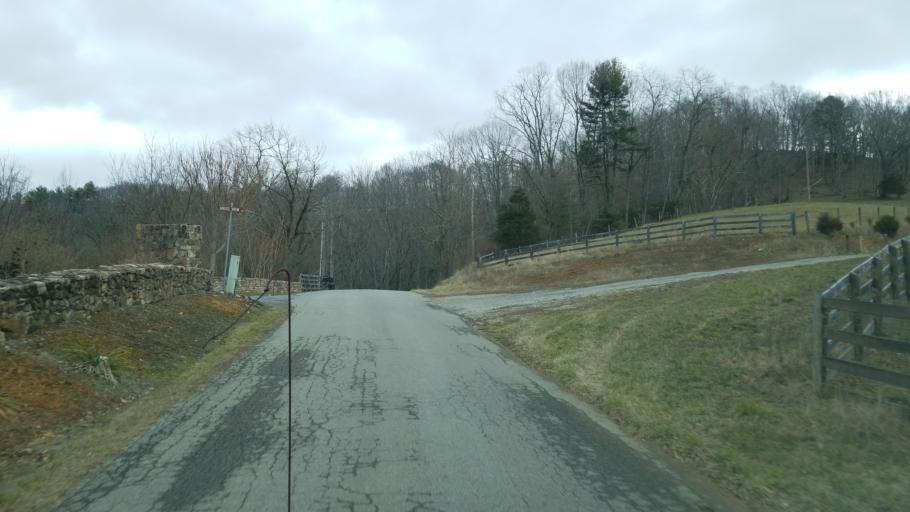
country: US
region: Virginia
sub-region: Giles County
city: Pearisburg
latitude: 37.2183
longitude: -80.7019
